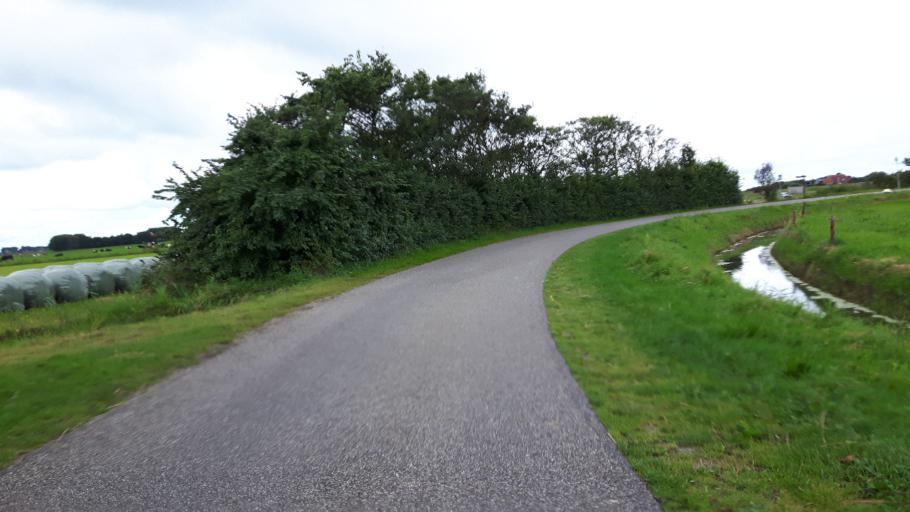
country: NL
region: Friesland
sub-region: Gemeente Ameland
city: Hollum
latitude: 53.4435
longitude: 5.6765
